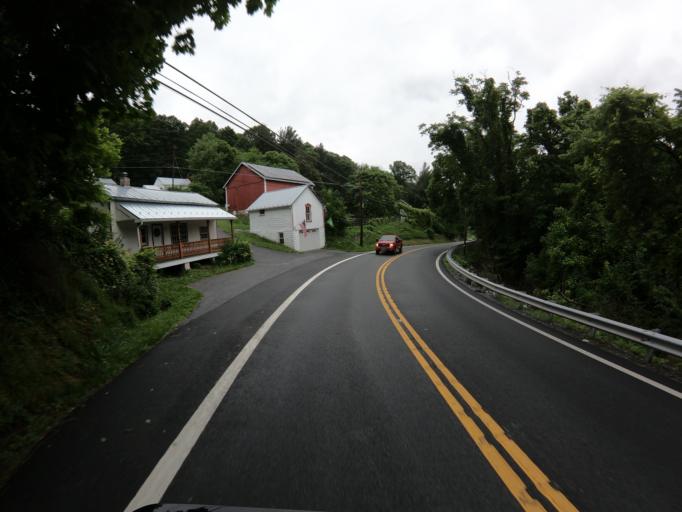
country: US
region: Maryland
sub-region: Washington County
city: Boonsboro
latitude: 39.4834
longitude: -77.6159
